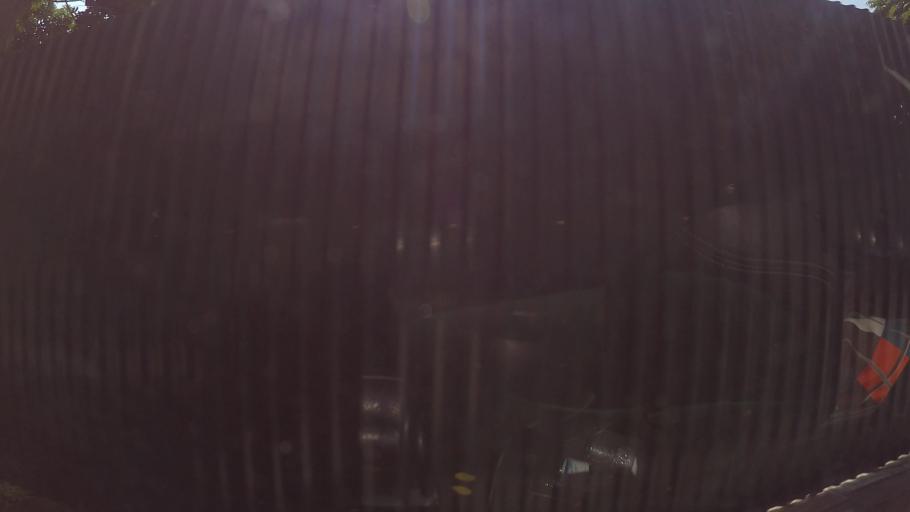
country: VN
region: Ha Noi
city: Trau Quy
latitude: 21.0279
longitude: 105.9086
